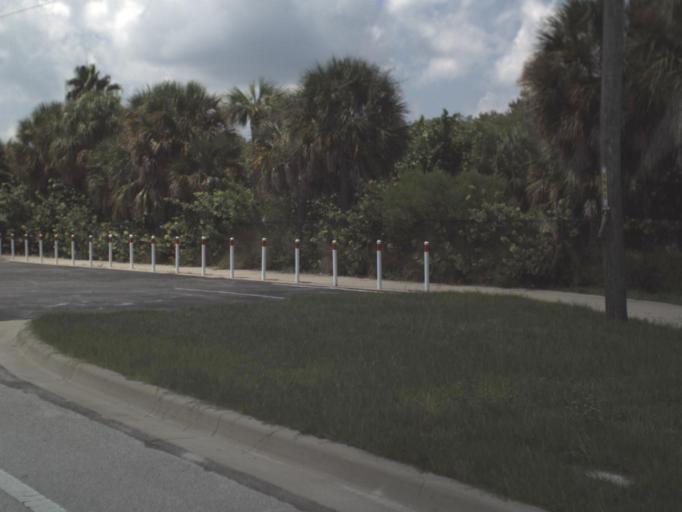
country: US
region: Florida
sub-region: Pinellas County
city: Tierra Verde
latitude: 27.6544
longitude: -82.7174
